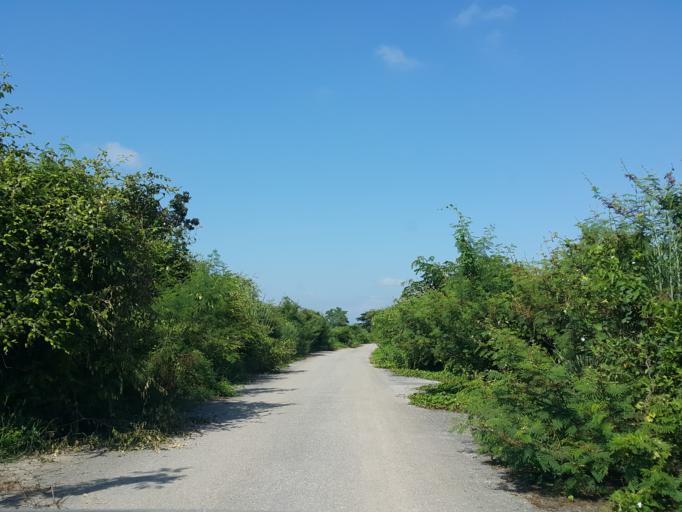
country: TH
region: Chiang Mai
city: Mae On
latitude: 18.8063
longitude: 99.1940
